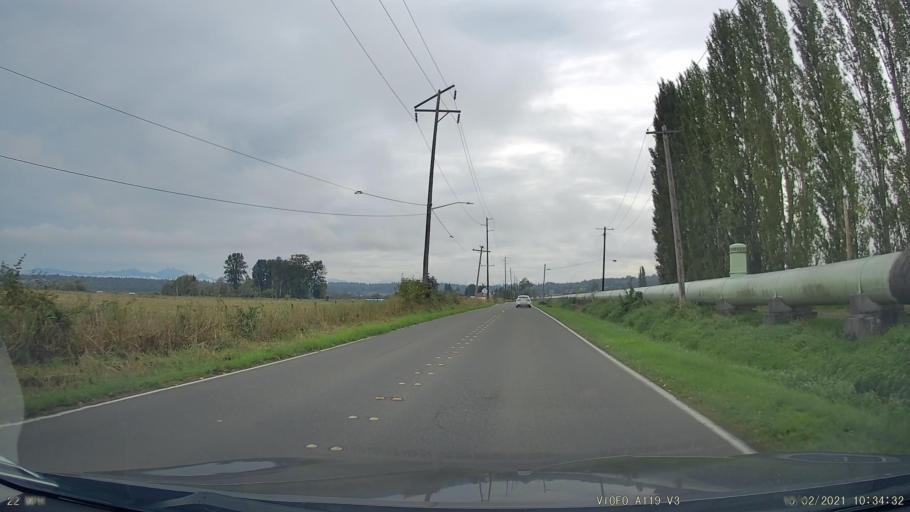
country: US
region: Washington
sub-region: Snohomish County
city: Everett
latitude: 47.9493
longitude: -122.1733
